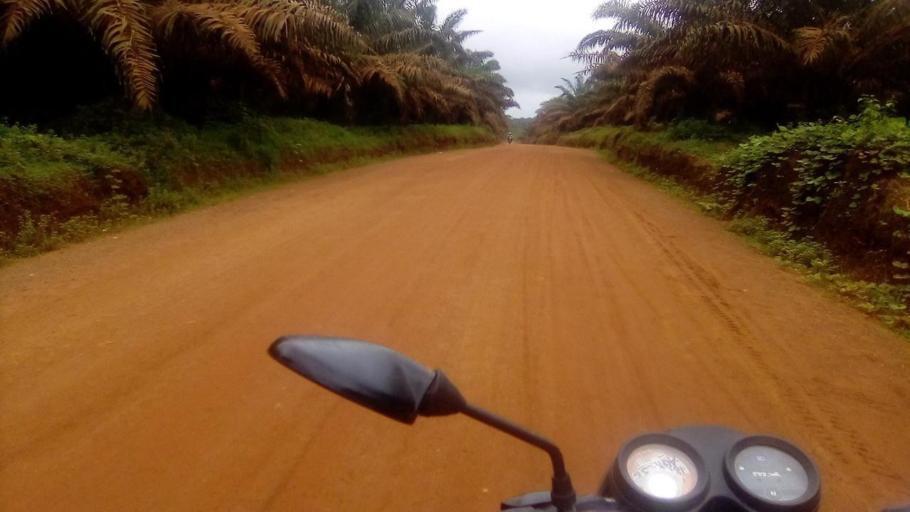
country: SL
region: Southern Province
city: Tongole
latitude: 7.4326
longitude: -11.8499
